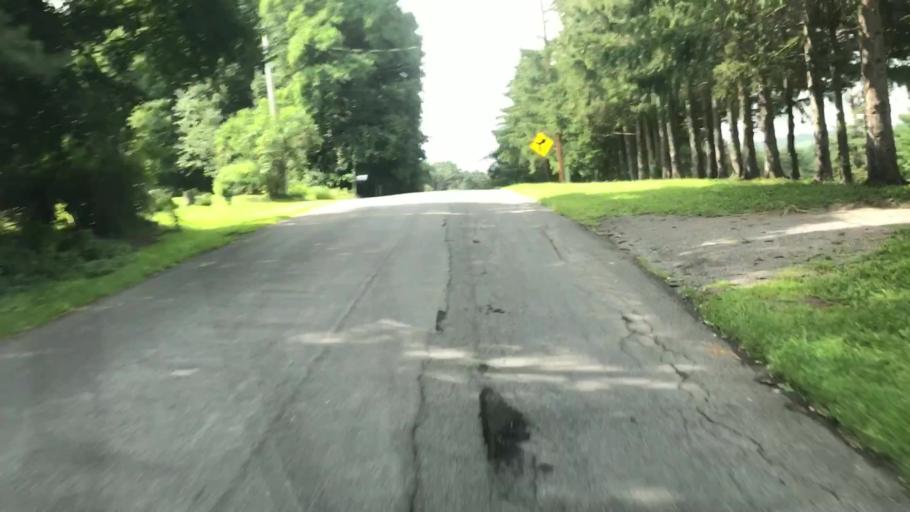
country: US
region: New York
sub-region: Onondaga County
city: Camillus
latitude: 43.0623
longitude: -76.3523
